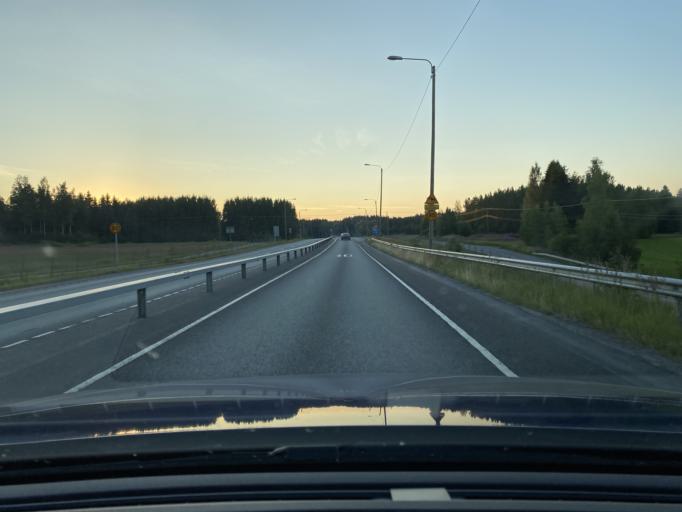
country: FI
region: Pirkanmaa
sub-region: Luoteis-Pirkanmaa
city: Ikaalinen
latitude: 61.7263
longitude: 23.1348
